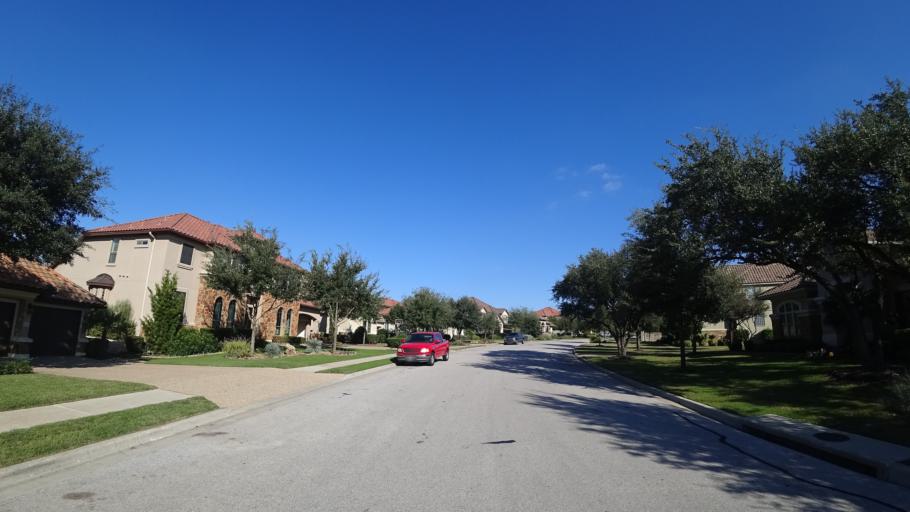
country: US
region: Texas
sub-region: Travis County
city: Bee Cave
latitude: 30.3479
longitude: -97.8942
